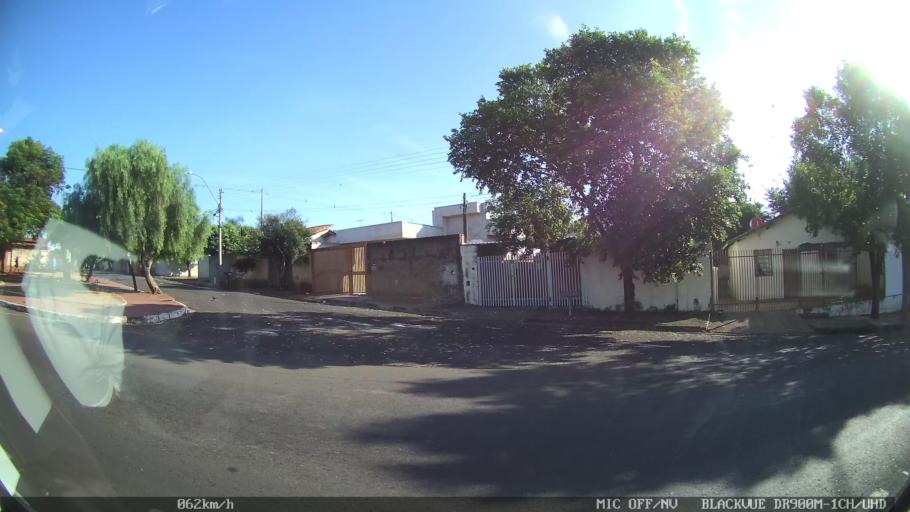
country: BR
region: Sao Paulo
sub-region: Sao Jose Do Rio Preto
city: Sao Jose do Rio Preto
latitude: -20.7647
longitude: -49.3803
